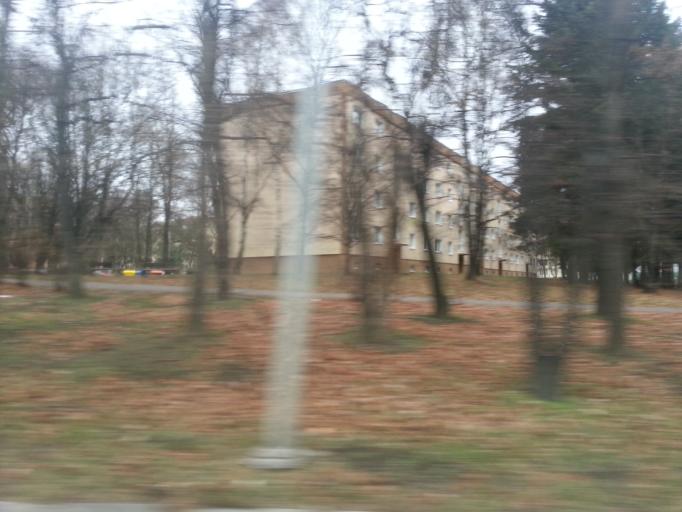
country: CZ
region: Central Bohemia
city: Horomerice
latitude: 50.0858
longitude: 14.3486
